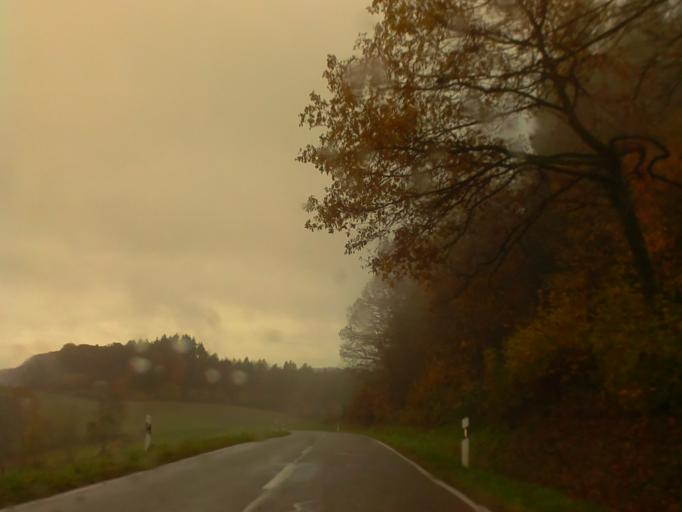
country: DE
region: Hesse
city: Neckarsteinach
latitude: 49.4109
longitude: 8.8497
